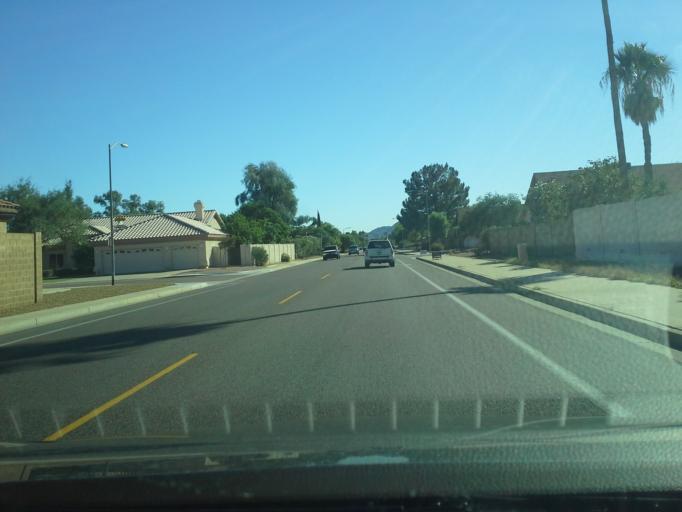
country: US
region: Arizona
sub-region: Maricopa County
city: Paradise Valley
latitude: 33.6249
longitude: -111.9866
